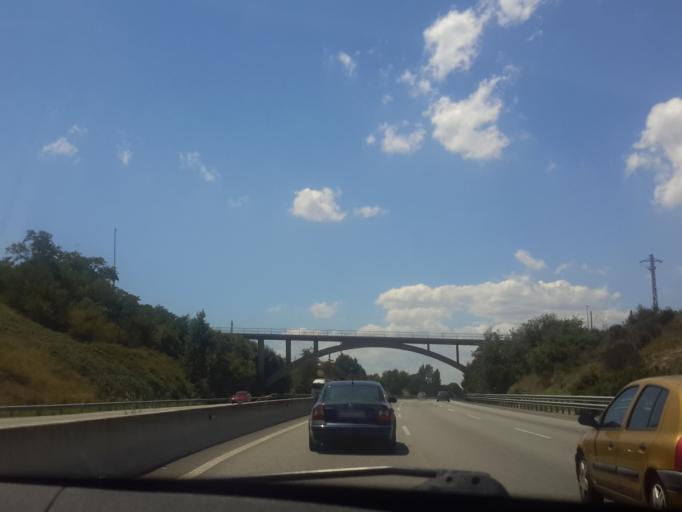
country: ES
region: Catalonia
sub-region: Provincia de Barcelona
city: Santa Maria de Palautordera
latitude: 41.6524
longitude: 2.4445
